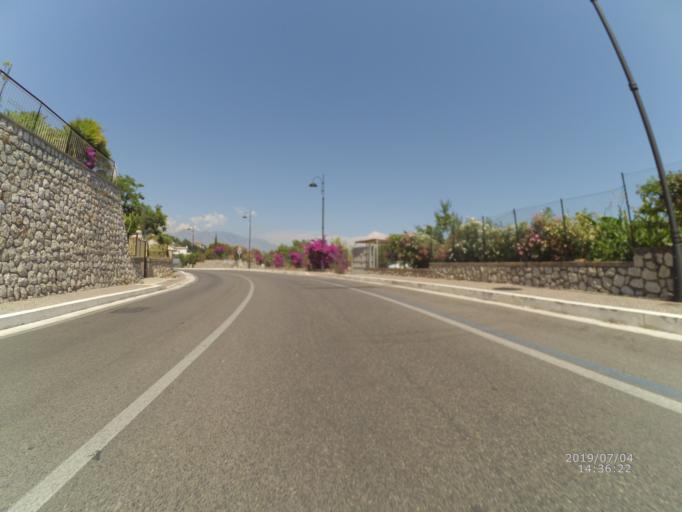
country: IT
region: Latium
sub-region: Provincia di Latina
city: Gaeta
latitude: 41.2097
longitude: 13.5537
